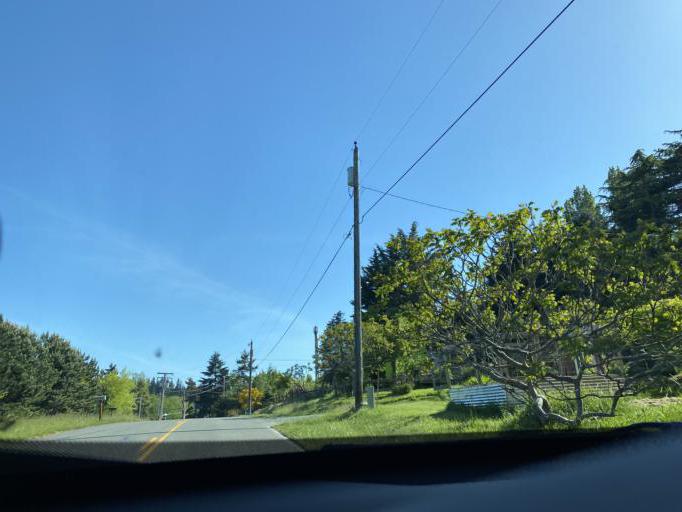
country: US
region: Washington
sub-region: Island County
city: Freeland
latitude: 48.0106
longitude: -122.5314
